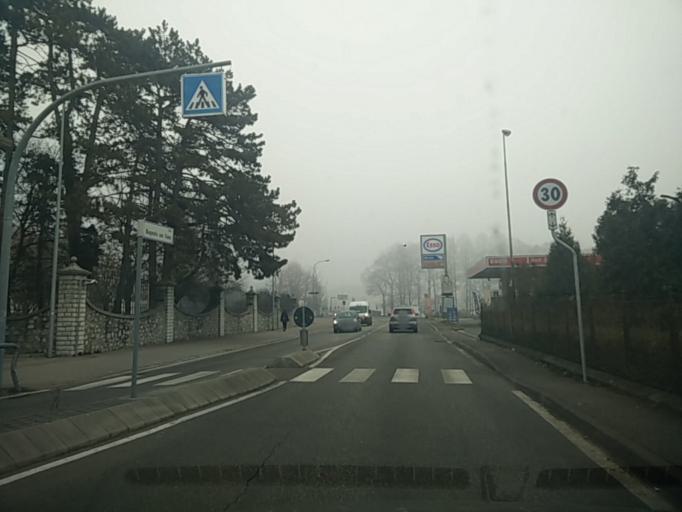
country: IT
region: Veneto
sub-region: Provincia di Belluno
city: Feltre
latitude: 46.0215
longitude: 11.9052
